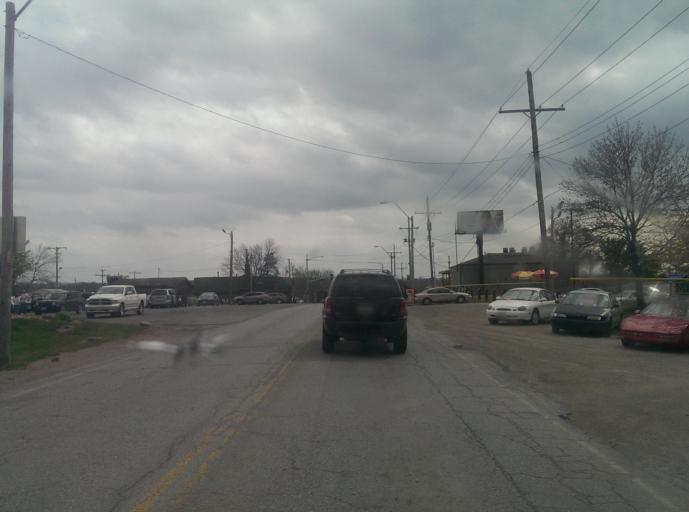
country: US
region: Missouri
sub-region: Jackson County
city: Grandview
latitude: 38.8838
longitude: -94.5865
